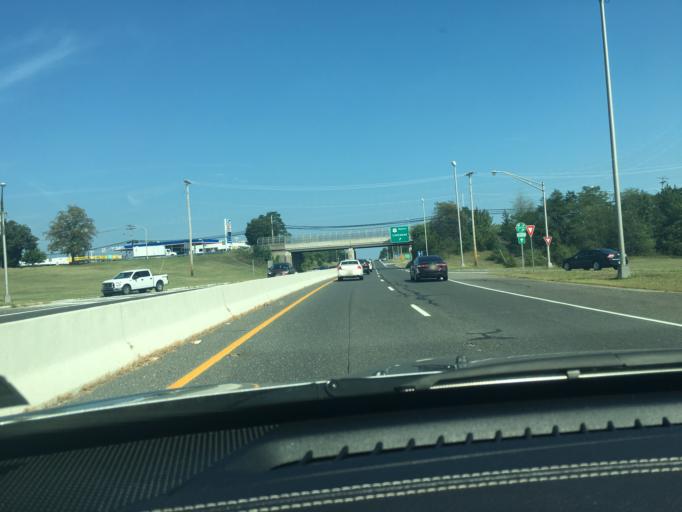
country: US
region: New Jersey
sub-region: Ocean County
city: Leisure Village
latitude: 40.0465
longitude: -74.2236
